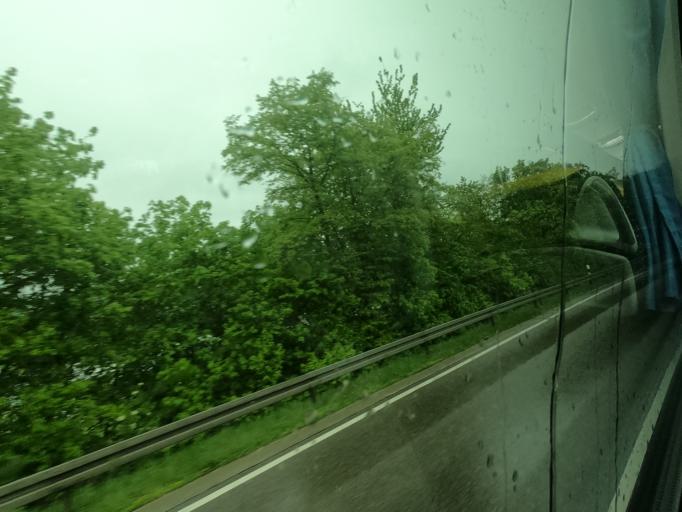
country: DE
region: Baden-Wuerttemberg
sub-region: Regierungsbezirk Stuttgart
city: Aalen
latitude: 48.8262
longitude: 10.1110
